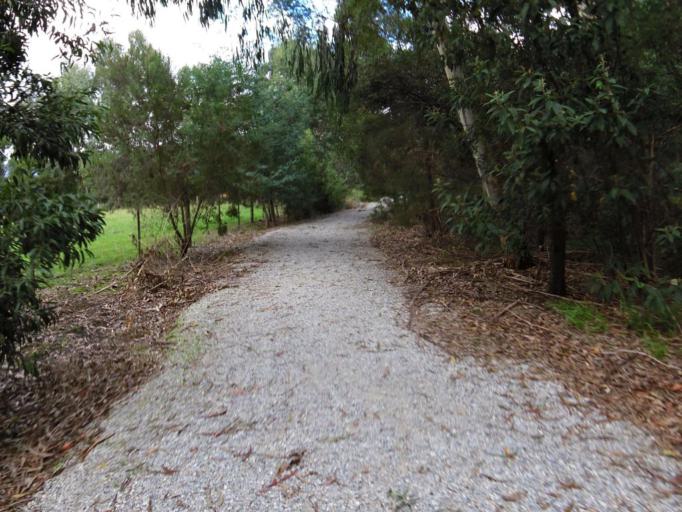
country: AU
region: Victoria
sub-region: Yarra Ranges
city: Mount Evelyn
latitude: -37.7789
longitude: 145.3612
